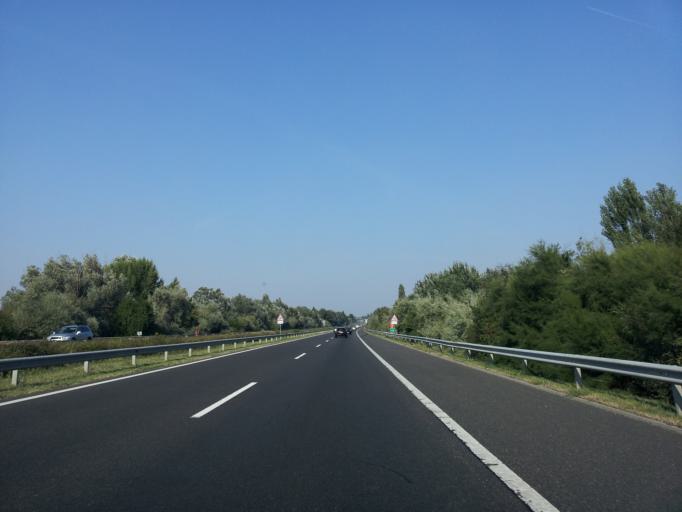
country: HU
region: Fejer
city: Szabadbattyan
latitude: 47.1344
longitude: 18.4143
